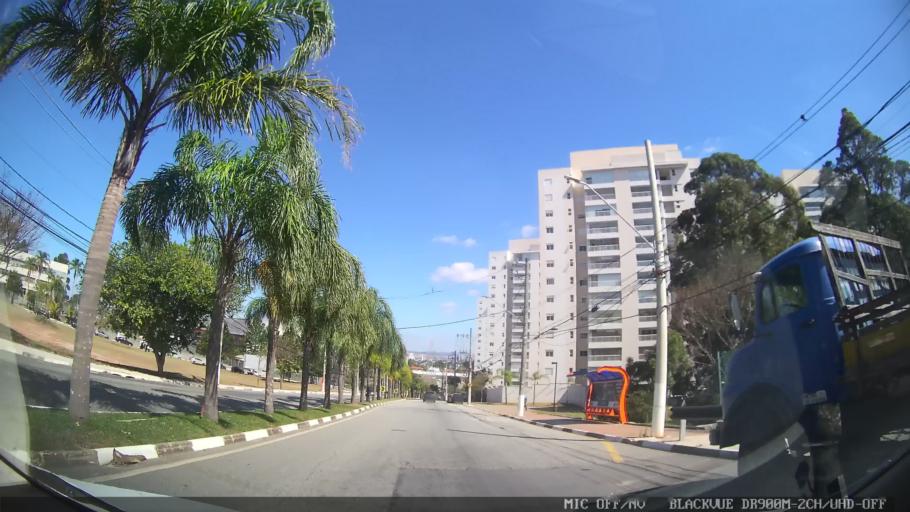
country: BR
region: Sao Paulo
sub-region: Carapicuiba
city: Carapicuiba
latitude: -23.4757
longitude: -46.8309
